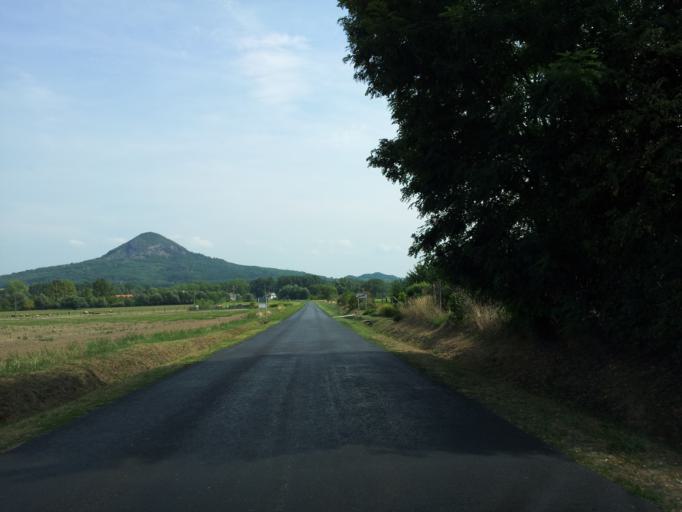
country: HU
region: Veszprem
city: Tapolca
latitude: 46.8412
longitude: 17.4689
